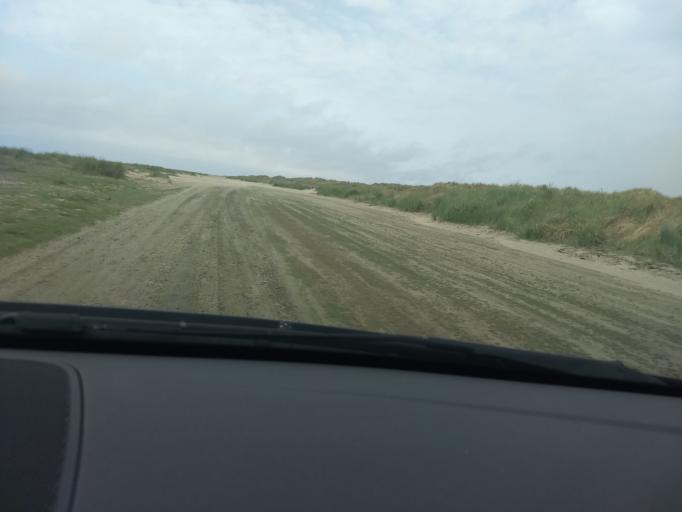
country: DK
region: South Denmark
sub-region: Fano Kommune
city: Nordby
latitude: 55.4099
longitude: 8.3850
